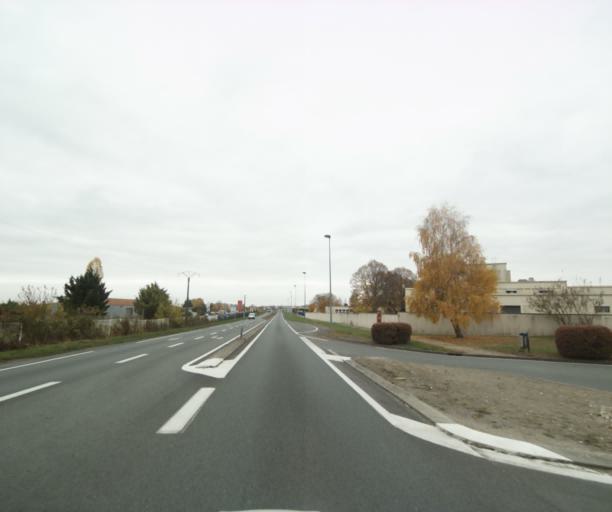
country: FR
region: Poitou-Charentes
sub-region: Departement de la Charente-Maritime
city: Les Gonds
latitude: 45.7093
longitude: -0.6292
